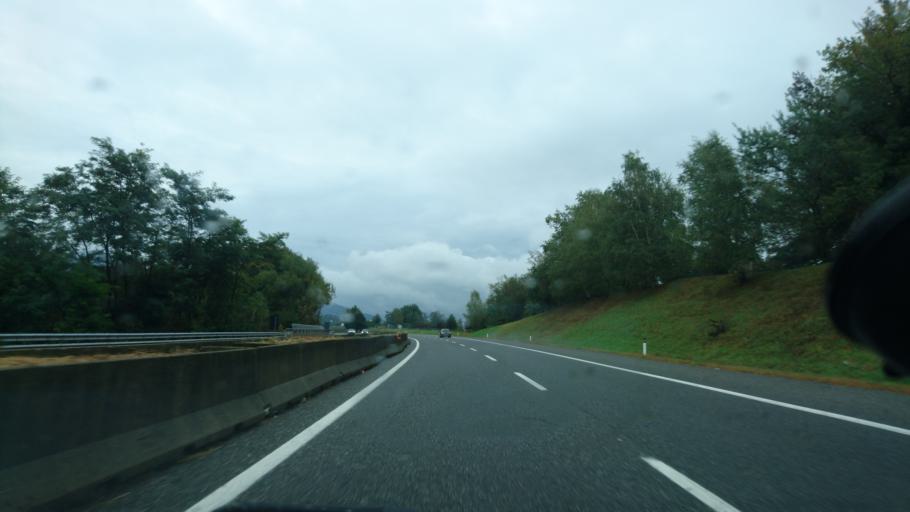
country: IT
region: Piedmont
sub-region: Provincia di Novara
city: Pisano
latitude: 45.7950
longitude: 8.5252
